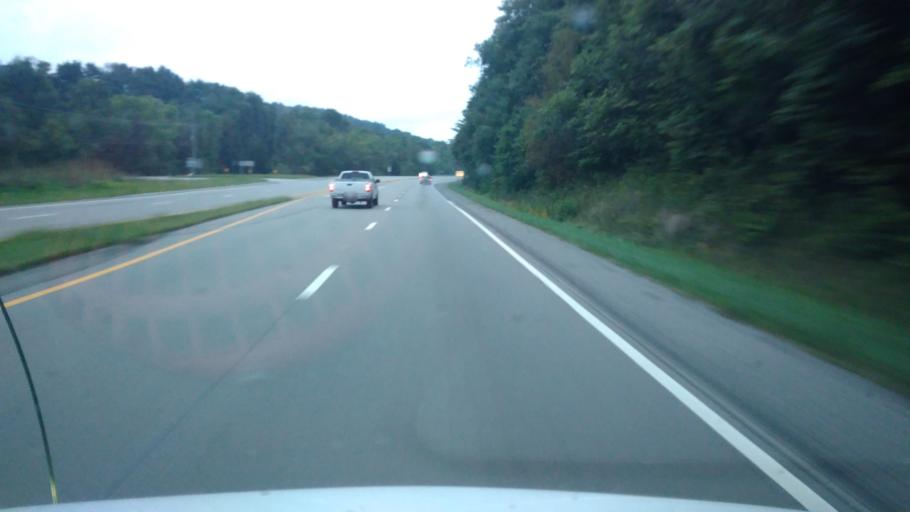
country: US
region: Ohio
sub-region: Ross County
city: Chillicothe
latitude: 39.2434
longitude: -82.9840
